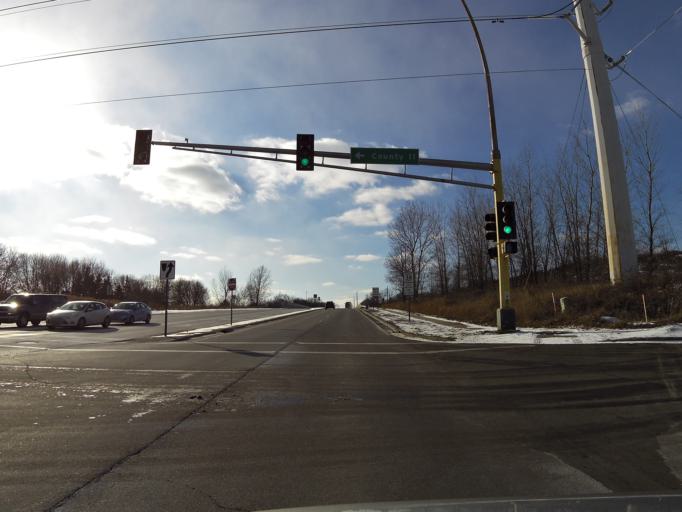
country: US
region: Minnesota
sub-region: Dakota County
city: Burnsville
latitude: 44.7539
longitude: -93.2582
